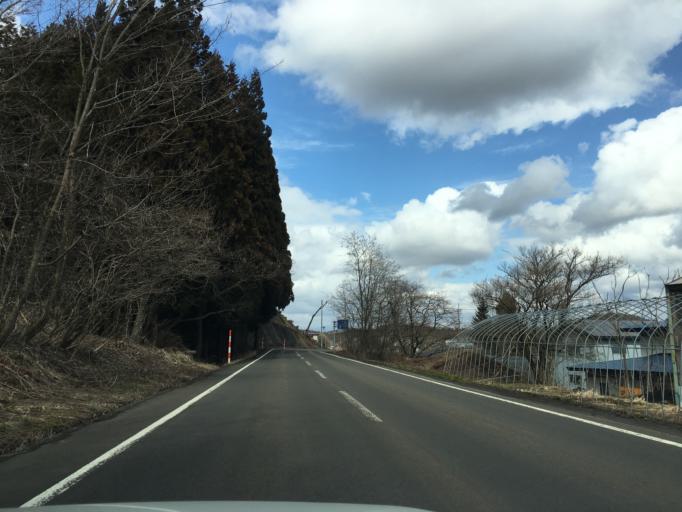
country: JP
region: Akita
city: Odate
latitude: 40.1974
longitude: 140.5348
